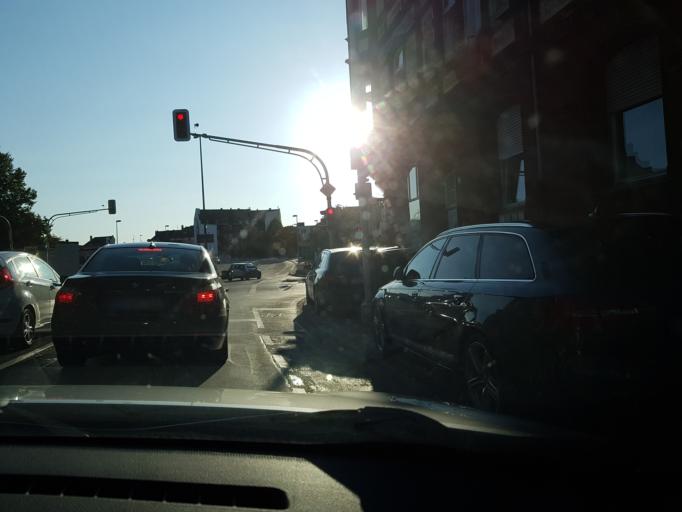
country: DE
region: Rheinland-Pfalz
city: Koblenz
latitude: 50.3668
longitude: 7.5952
